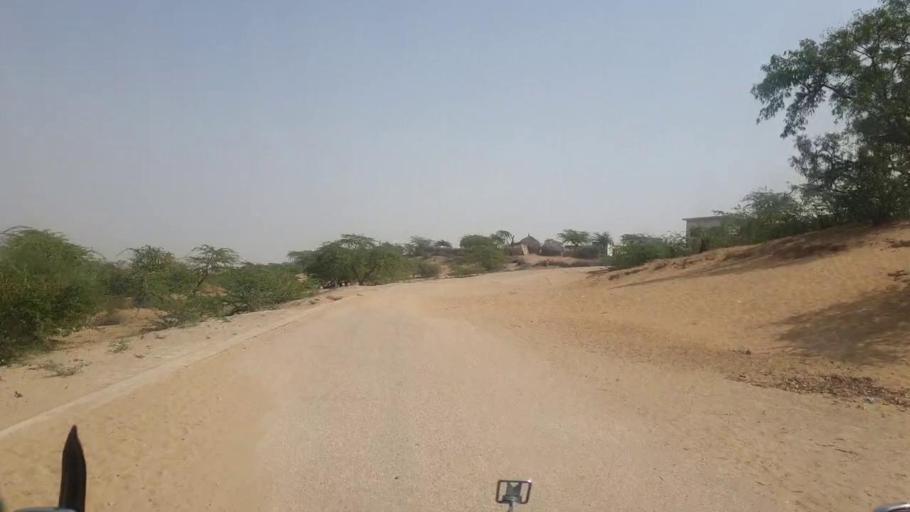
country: PK
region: Sindh
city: Umarkot
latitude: 25.2320
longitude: 70.2477
